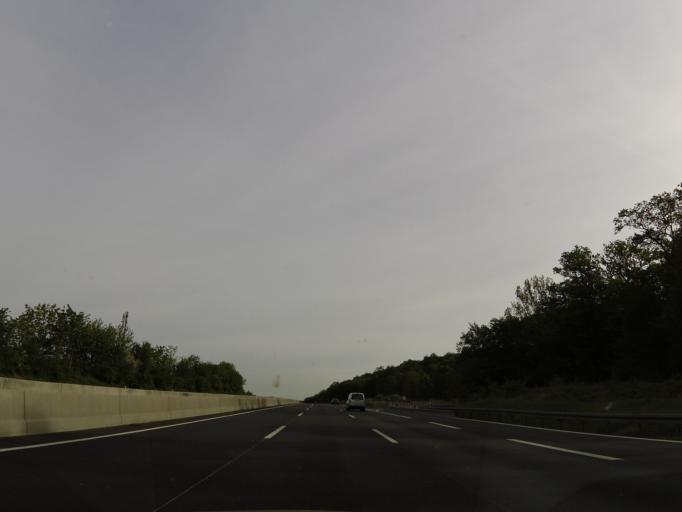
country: DE
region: Lower Saxony
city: Haverlah
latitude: 52.0572
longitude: 10.1915
